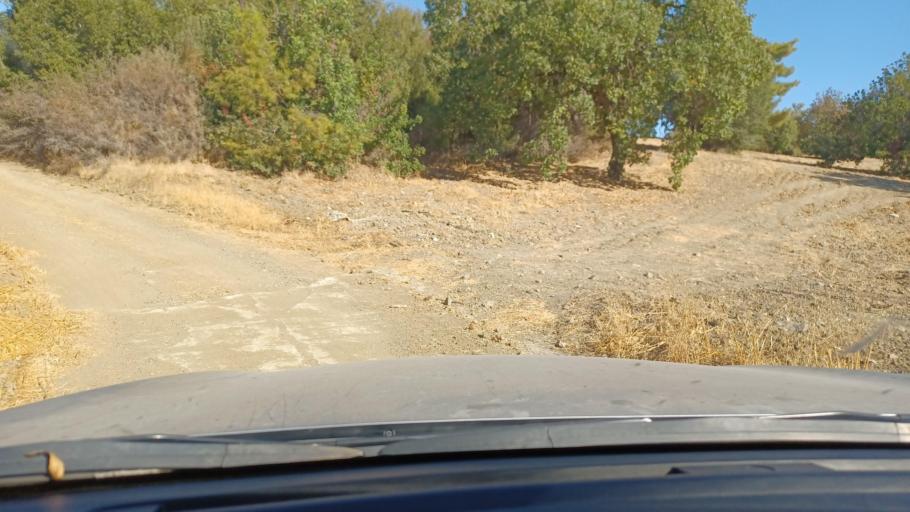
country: CY
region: Pafos
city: Polis
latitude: 35.0109
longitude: 32.5038
